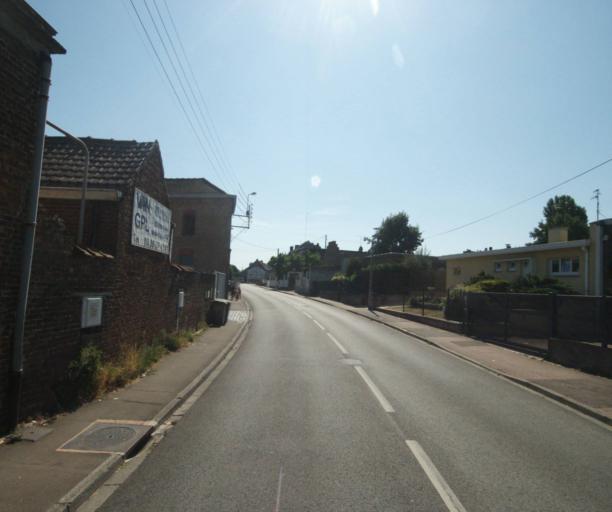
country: FR
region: Nord-Pas-de-Calais
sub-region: Departement du Nord
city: Halluin
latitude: 50.7774
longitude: 3.1314
